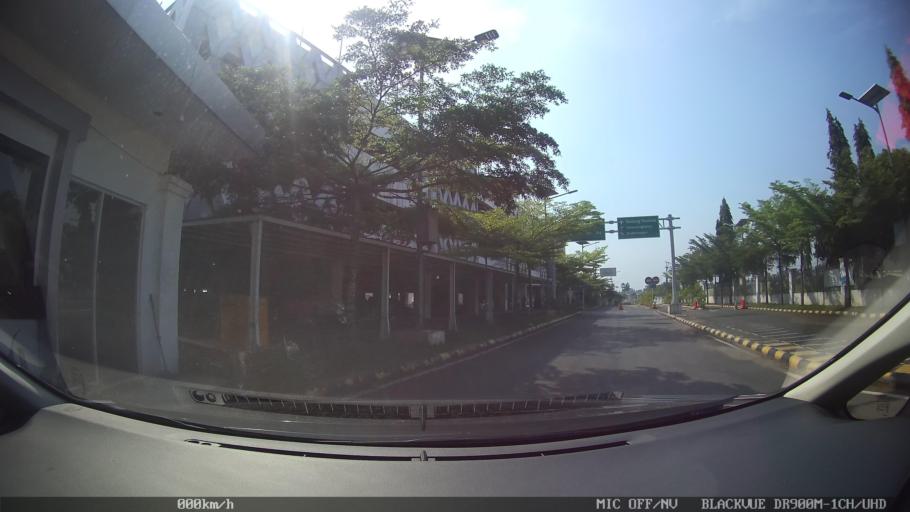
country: ID
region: Lampung
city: Natar
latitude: -5.2409
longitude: 105.1741
